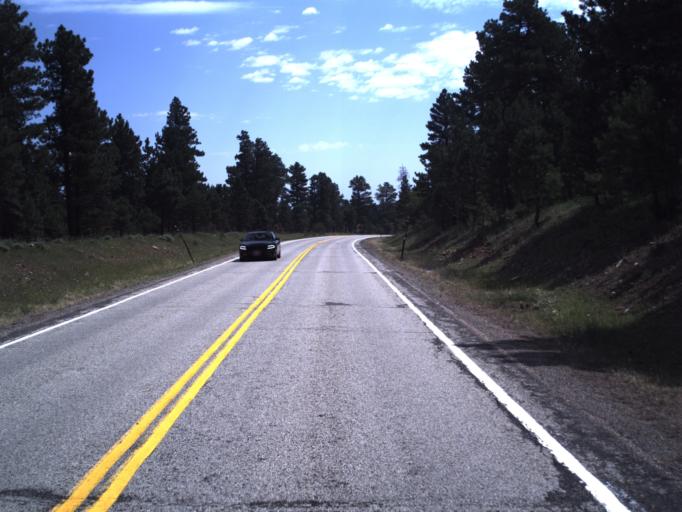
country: US
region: Utah
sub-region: Daggett County
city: Manila
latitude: 40.8605
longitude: -109.5476
